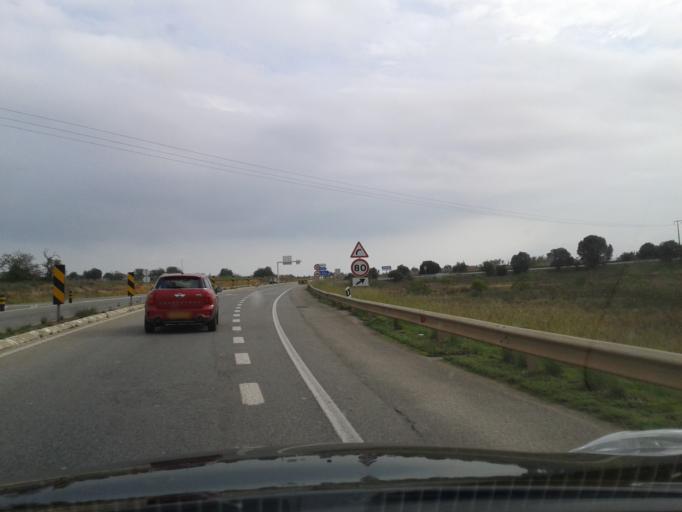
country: PT
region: Faro
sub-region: Albufeira
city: Ferreiras
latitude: 37.1277
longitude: -8.2570
